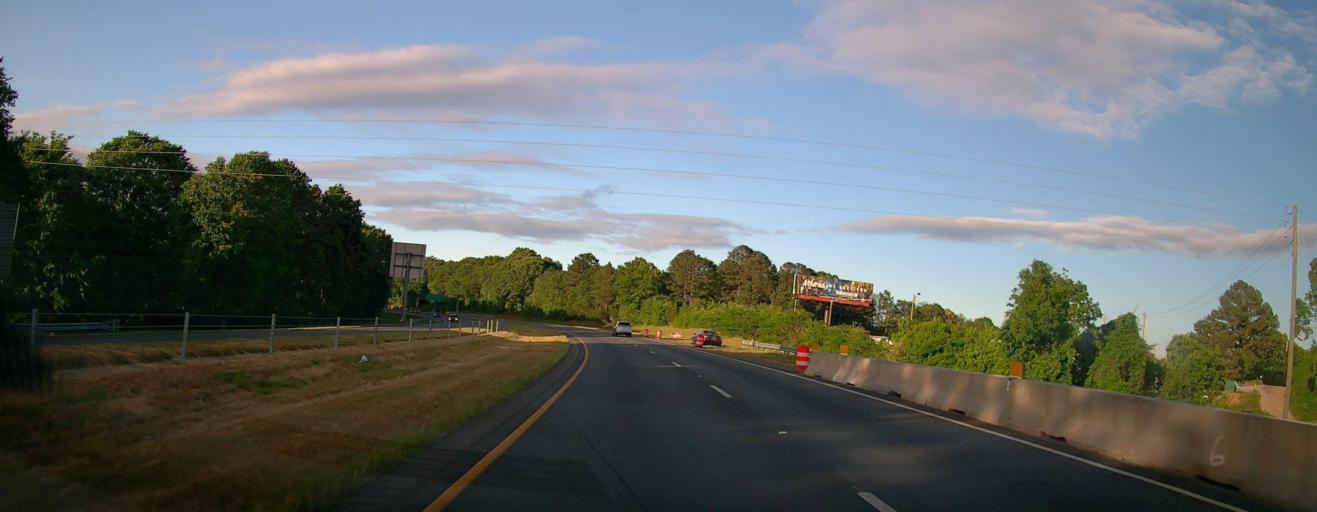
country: US
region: Georgia
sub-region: Clarke County
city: Athens
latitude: 33.9500
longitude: -83.3514
